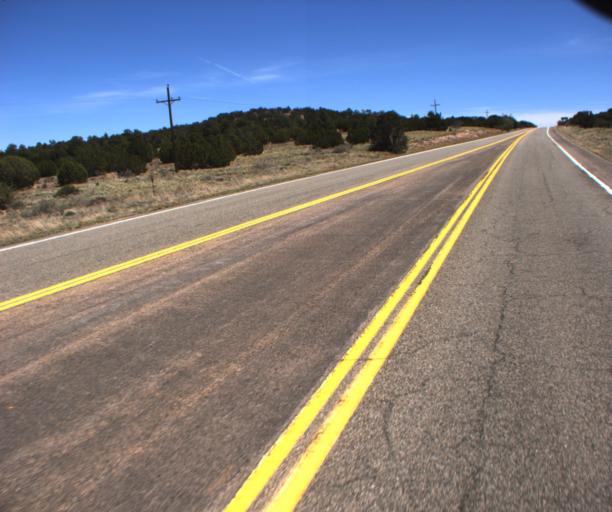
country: US
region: Arizona
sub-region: Mohave County
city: Peach Springs
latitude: 35.5283
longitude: -113.2249
